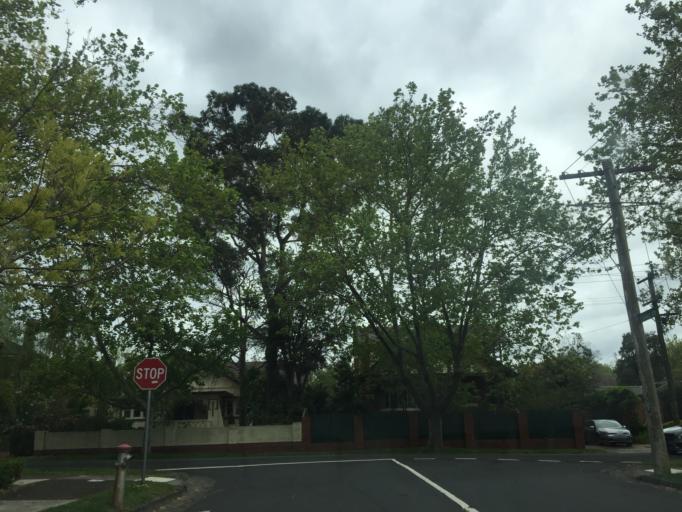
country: AU
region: Victoria
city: Balwyn
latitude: -37.8136
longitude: 145.0545
